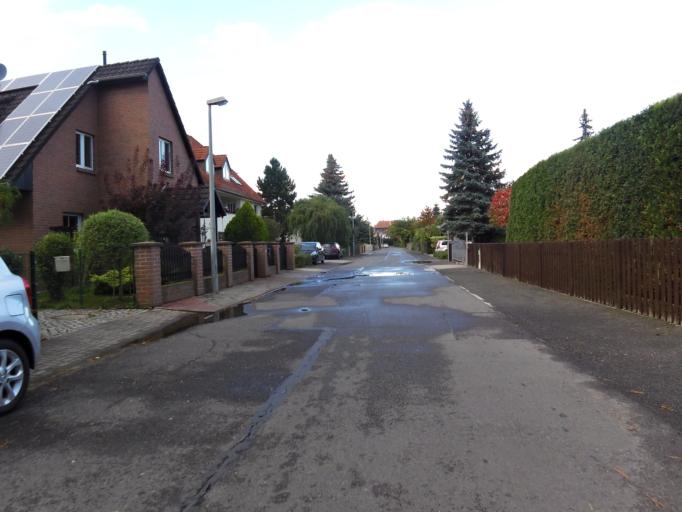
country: DE
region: Saxony
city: Grossposna
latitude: 51.3215
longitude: 12.4765
